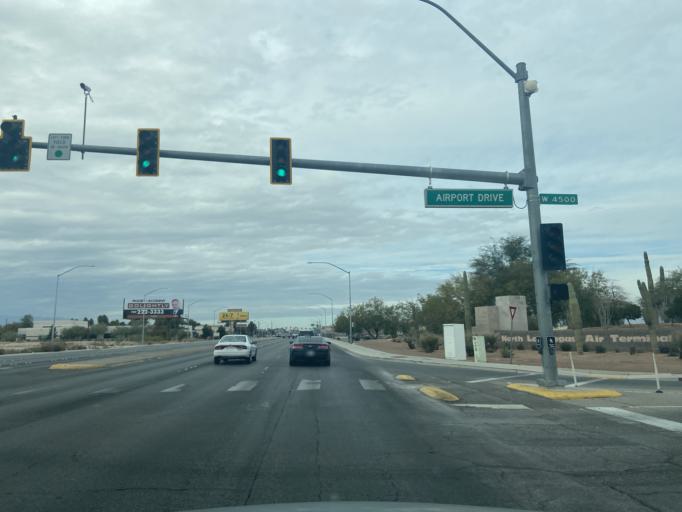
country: US
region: Nevada
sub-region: Clark County
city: Las Vegas
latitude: 36.2068
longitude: -115.2025
